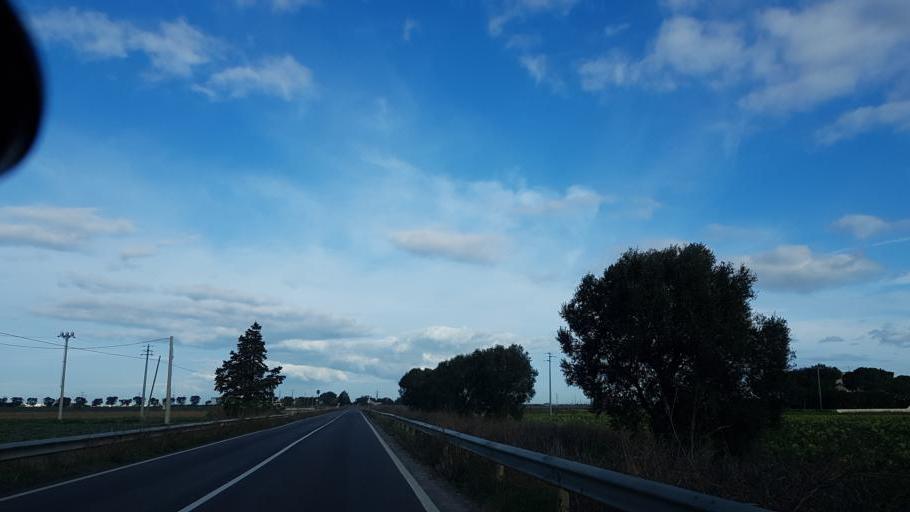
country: IT
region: Apulia
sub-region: Provincia di Brindisi
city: Tuturano
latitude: 40.5728
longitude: 17.9676
